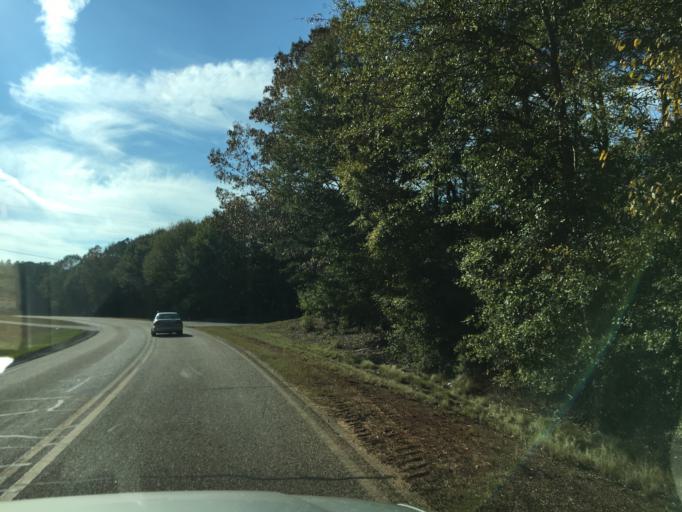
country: US
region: Georgia
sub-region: Hart County
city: Hartwell
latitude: 34.3027
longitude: -82.8334
